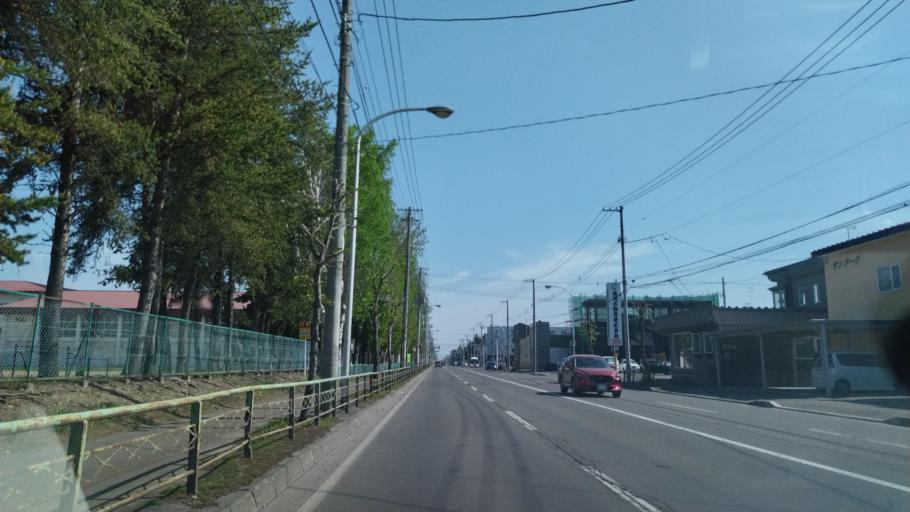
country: JP
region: Hokkaido
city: Obihiro
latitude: 42.9065
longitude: 143.1994
